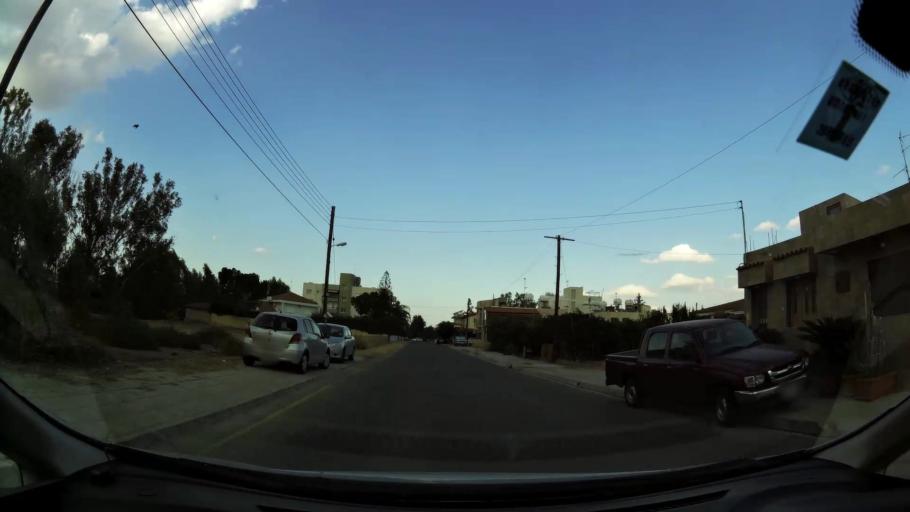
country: CY
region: Lefkosia
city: Kato Deftera
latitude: 35.1129
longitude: 33.3027
